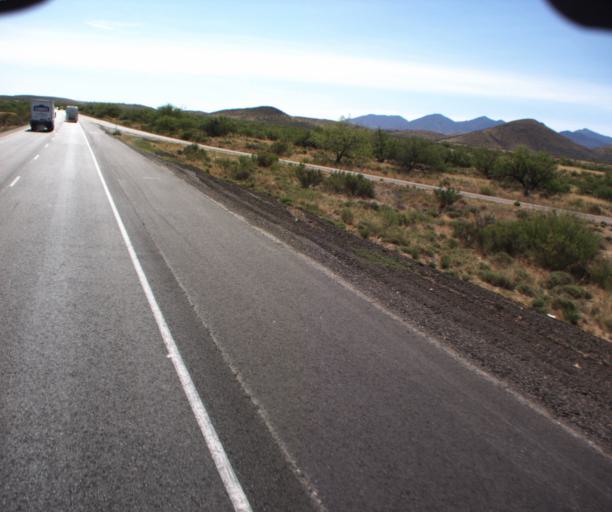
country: US
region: Arizona
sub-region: Cochise County
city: Mescal
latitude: 31.9760
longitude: -110.5103
